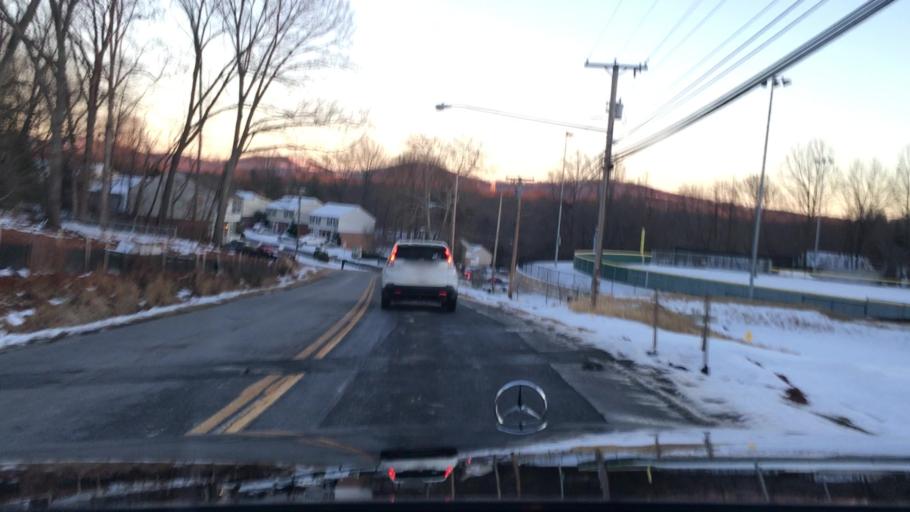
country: US
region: Virginia
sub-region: City of Lynchburg
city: West Lynchburg
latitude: 37.3626
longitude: -79.2036
